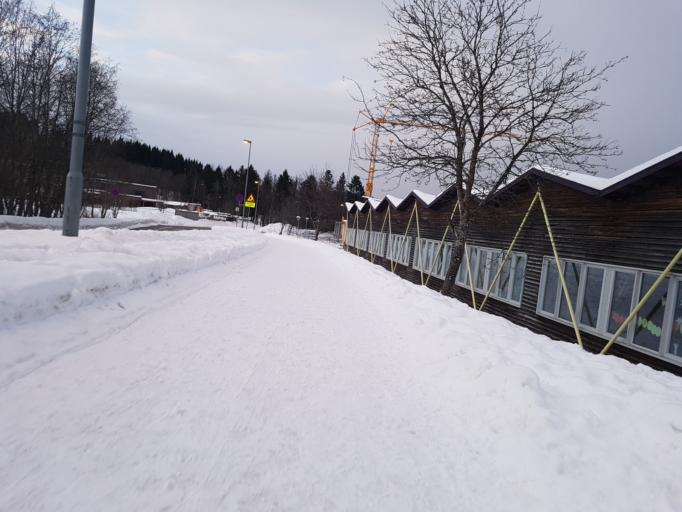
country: NO
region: Sor-Trondelag
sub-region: Trondheim
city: Trondheim
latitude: 63.3808
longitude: 10.3798
